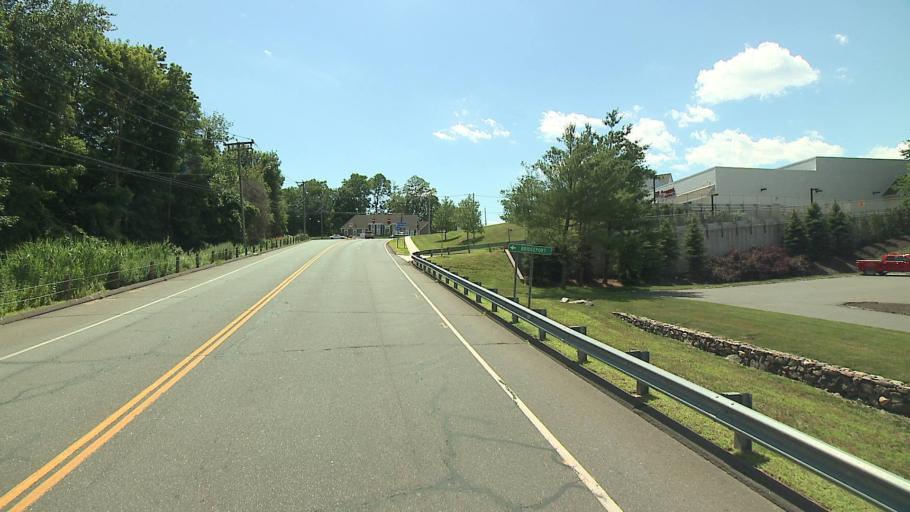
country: US
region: Connecticut
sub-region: Fairfield County
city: Newtown
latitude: 41.4019
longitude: -73.2957
